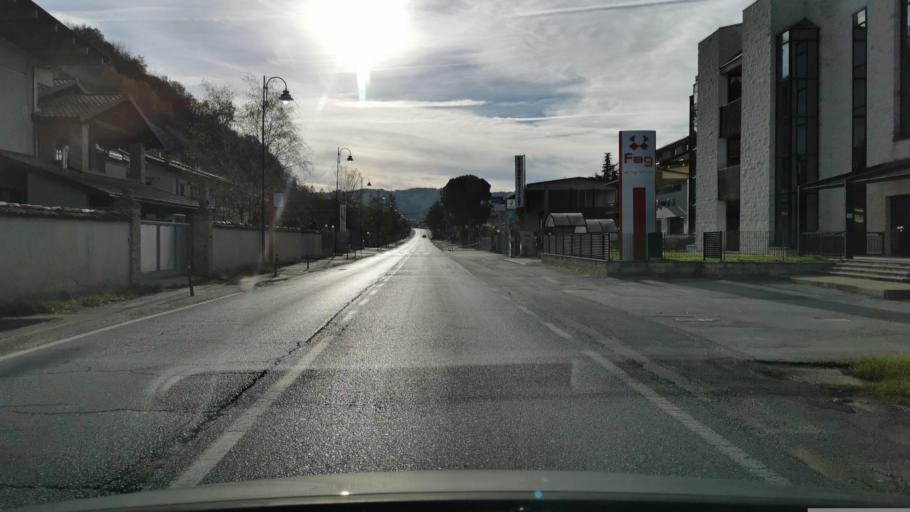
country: IT
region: Piedmont
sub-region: Provincia di Cuneo
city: Dogliani
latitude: 44.5408
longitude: 7.9297
